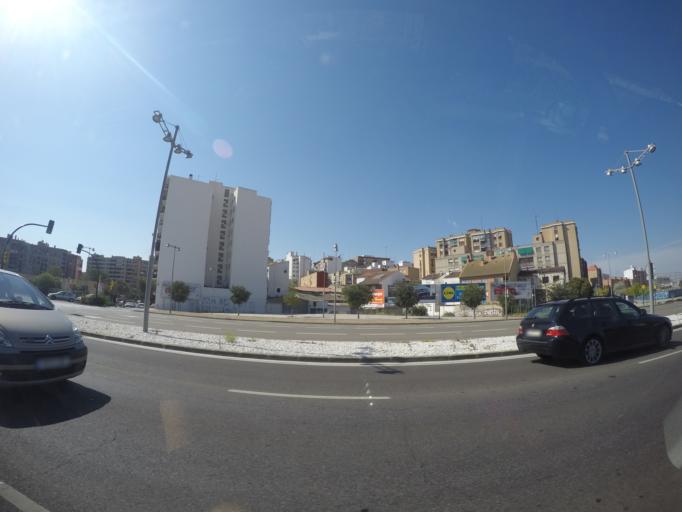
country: ES
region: Aragon
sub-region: Provincia de Zaragoza
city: Almozara
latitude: 41.6567
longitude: -0.9002
